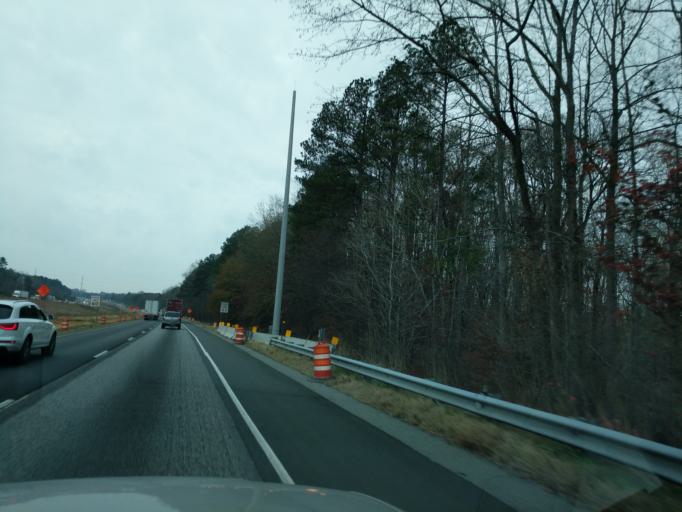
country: US
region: Georgia
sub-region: Gwinnett County
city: Sugar Hill
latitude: 34.0546
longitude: -84.0095
